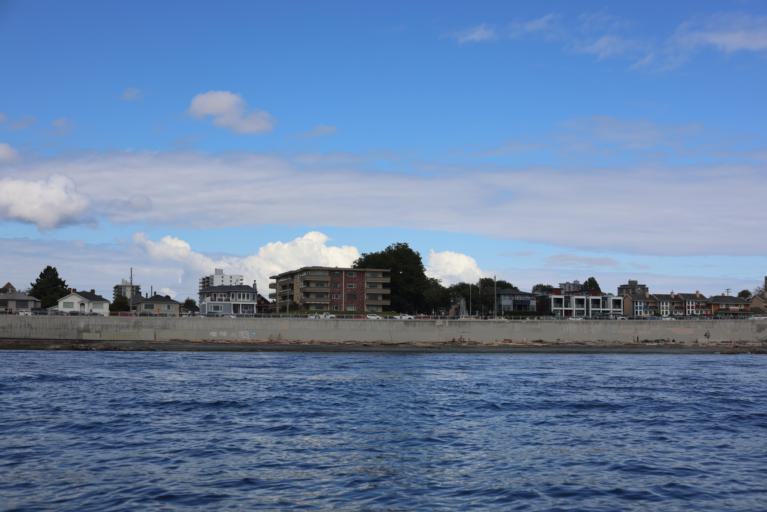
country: CA
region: British Columbia
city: Victoria
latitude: 48.4119
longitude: -123.3830
